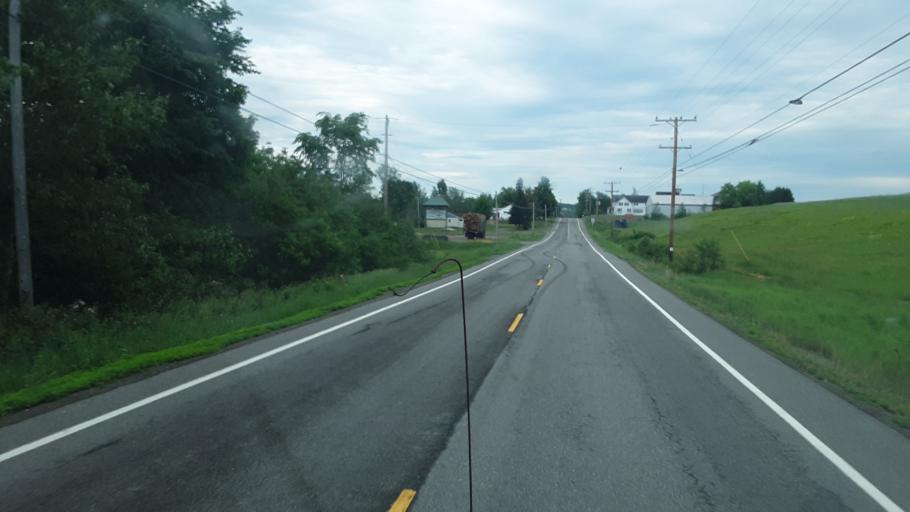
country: US
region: Maine
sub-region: Penobscot County
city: Patten
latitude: 46.0087
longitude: -68.4465
